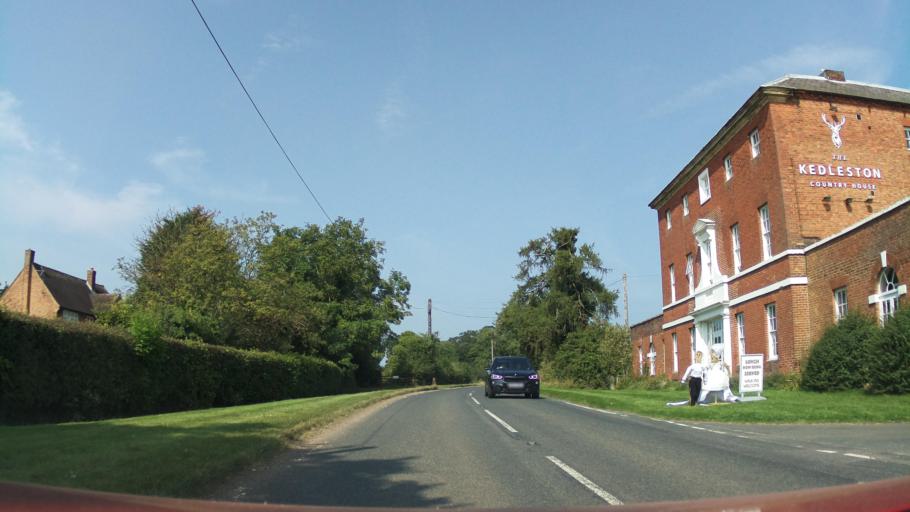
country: GB
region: England
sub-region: Derbyshire
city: Duffield
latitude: 52.9614
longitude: -1.5158
